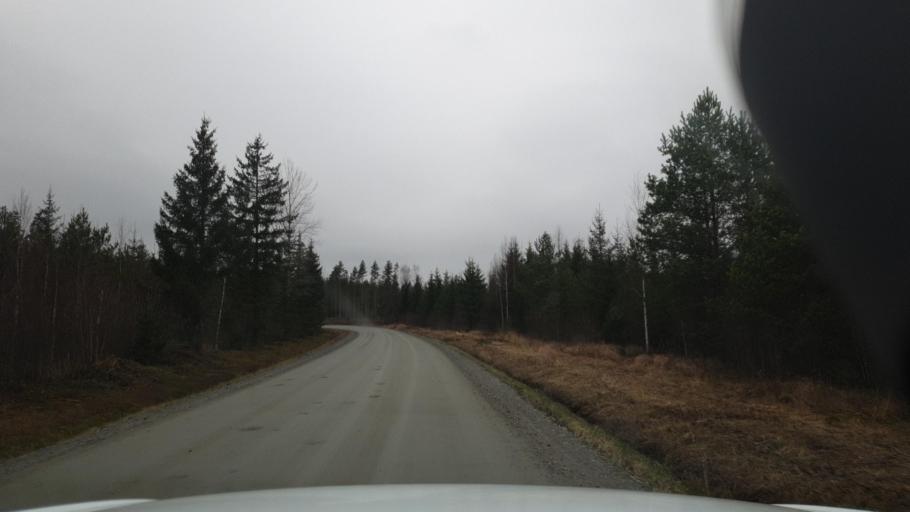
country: SE
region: Vaermland
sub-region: Karlstads Kommun
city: Edsvalla
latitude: 59.4459
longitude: 13.1648
